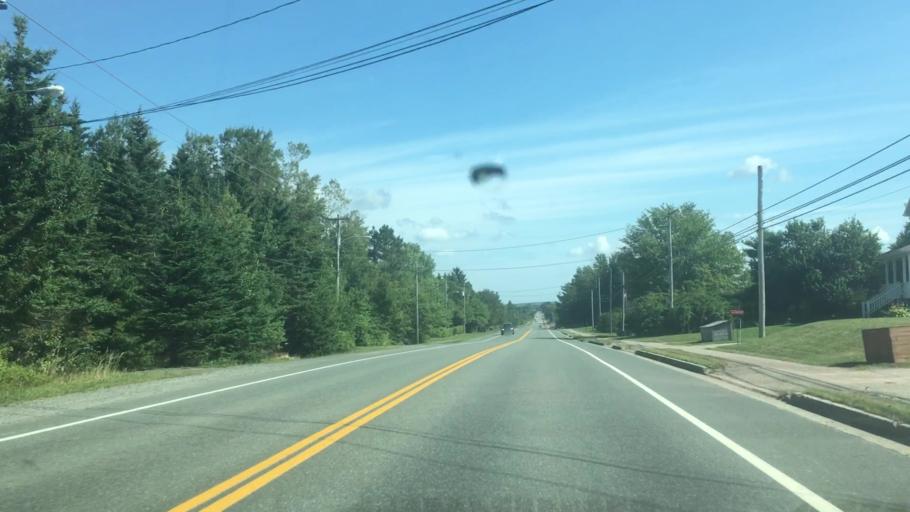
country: CA
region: Nova Scotia
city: Sydney
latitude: 46.0519
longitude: -60.3191
